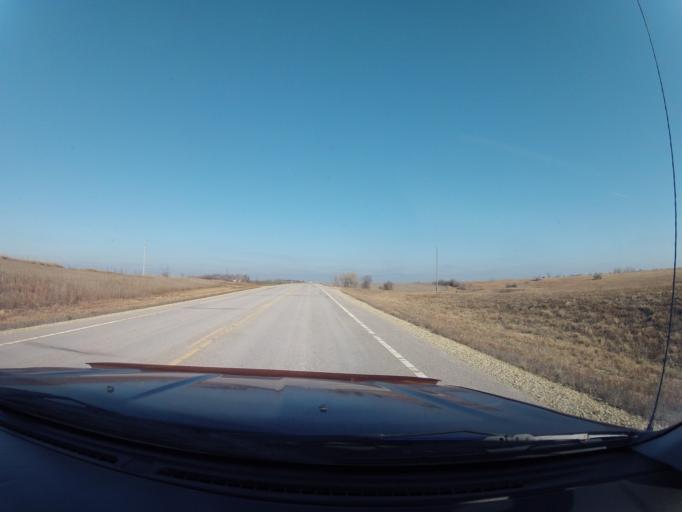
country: US
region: Kansas
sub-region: Marshall County
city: Blue Rapids
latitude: 39.5418
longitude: -96.7552
